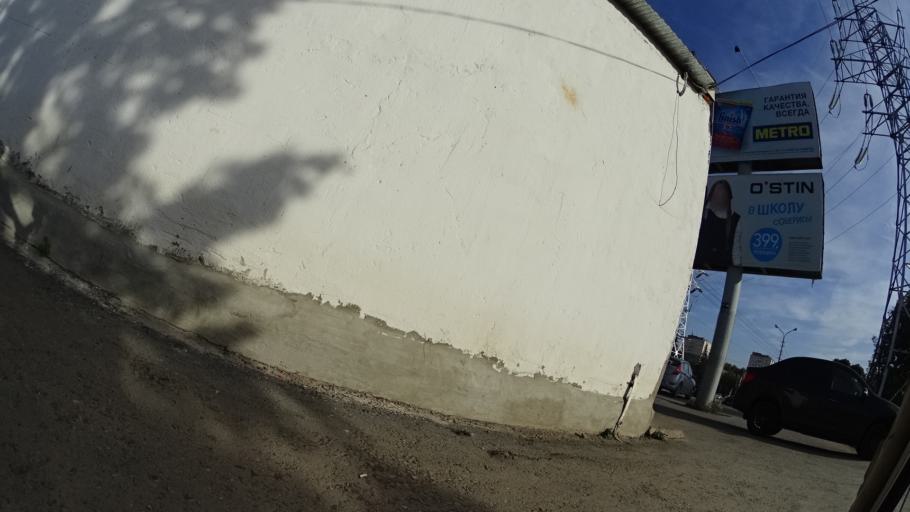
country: RU
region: Bashkortostan
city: Ufa
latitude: 54.7387
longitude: 55.9728
